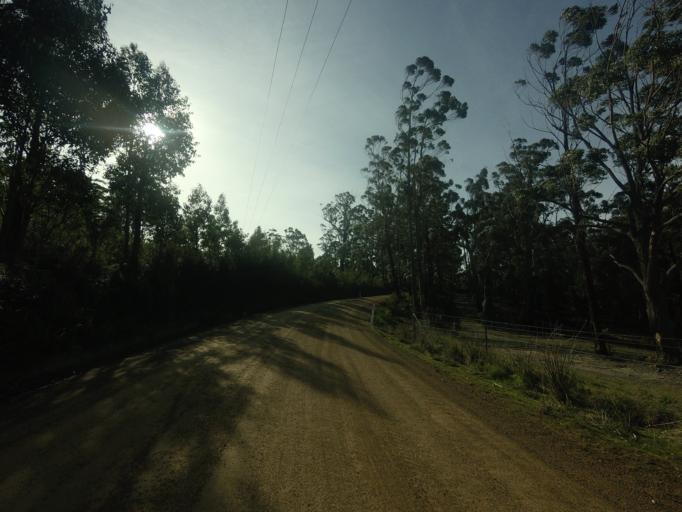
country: AU
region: Tasmania
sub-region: Kingborough
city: Kettering
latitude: -43.0923
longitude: 147.2650
